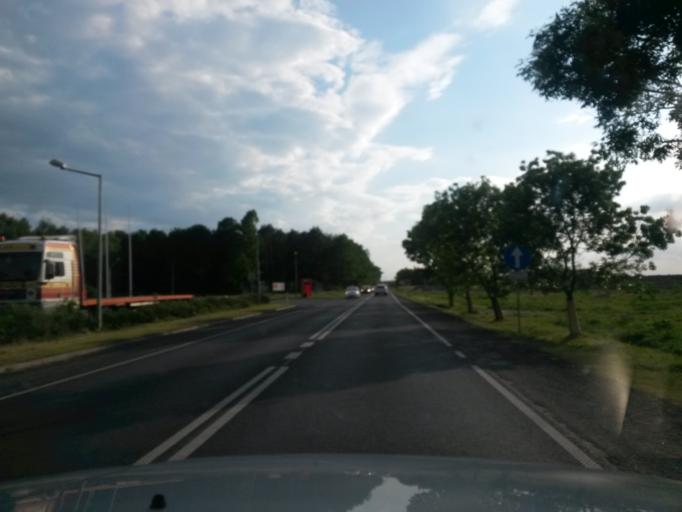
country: PL
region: Lodz Voivodeship
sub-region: Powiat belchatowski
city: Belchatow
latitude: 51.3922
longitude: 19.4055
